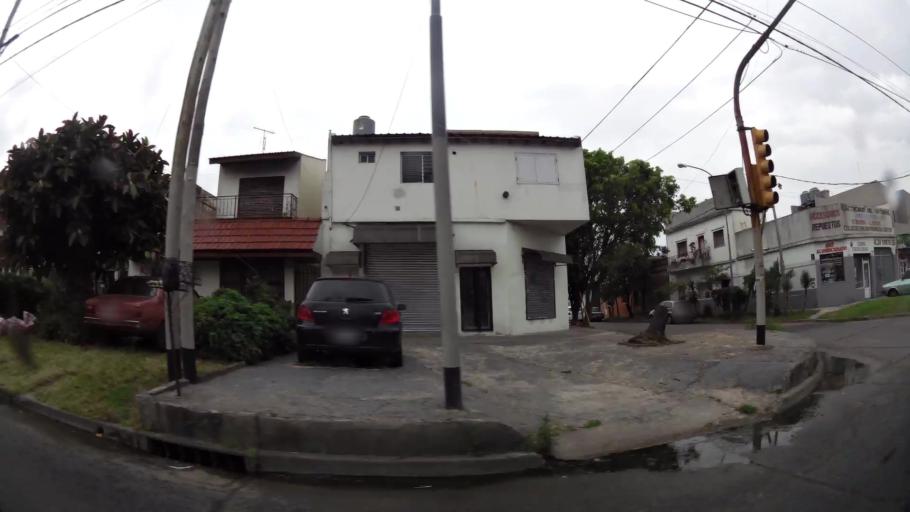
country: AR
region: Buenos Aires
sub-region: Partido de Lanus
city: Lanus
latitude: -34.6875
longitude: -58.3994
